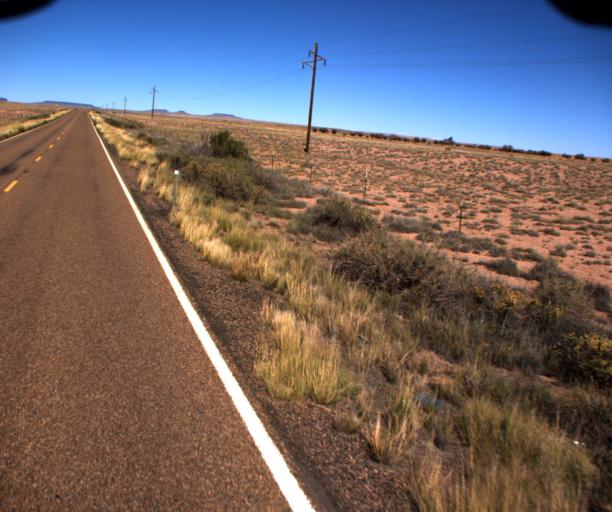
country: US
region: Arizona
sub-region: Navajo County
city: Holbrook
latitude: 35.0830
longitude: -110.0984
